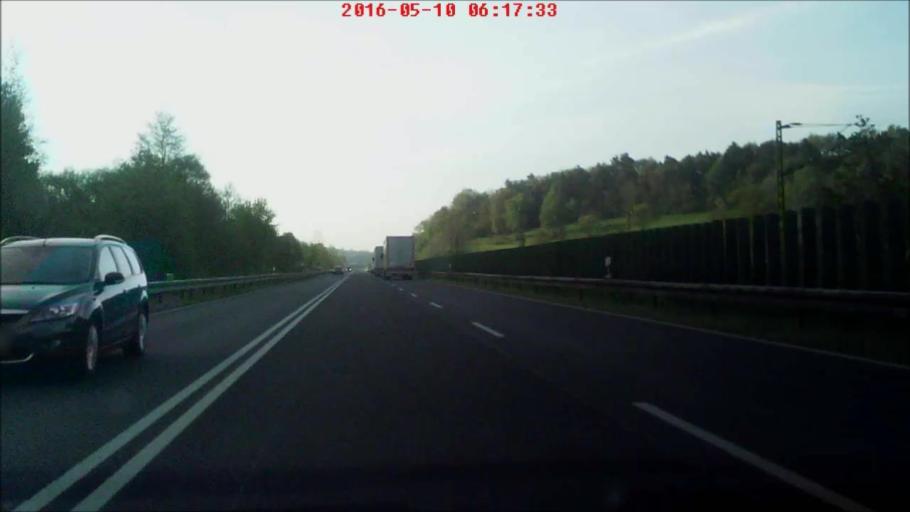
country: DE
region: Hesse
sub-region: Regierungsbezirk Kassel
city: Burghaun
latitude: 50.7331
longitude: 9.6966
